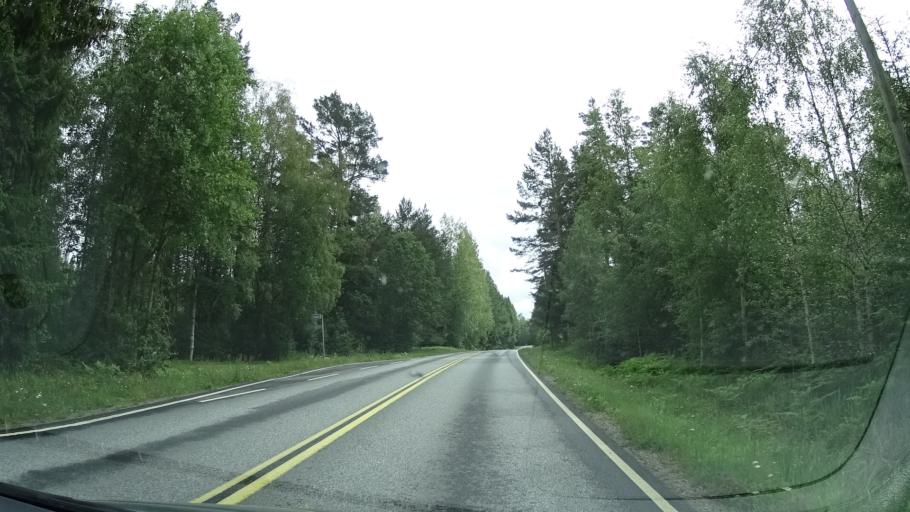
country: FI
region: Pirkanmaa
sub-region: Etelae-Pirkanmaa
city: Urjala
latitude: 61.0894
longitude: 23.3945
